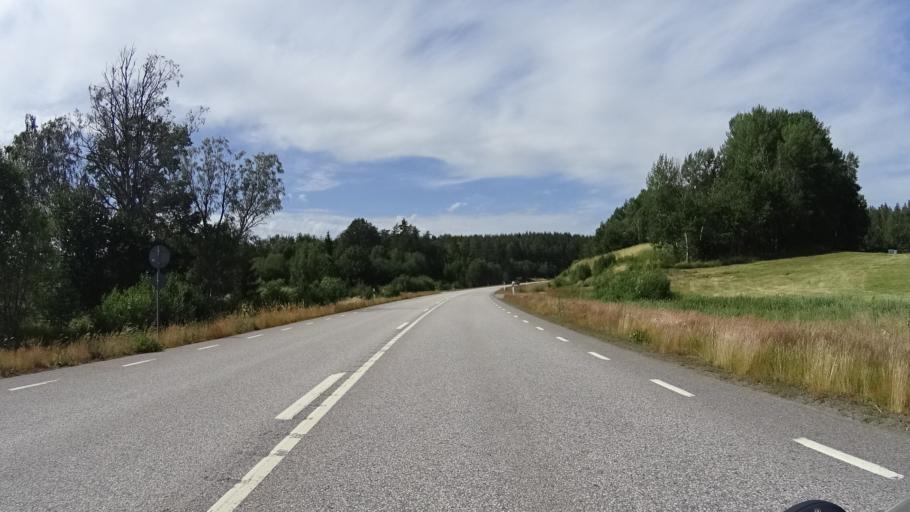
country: SE
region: Kalmar
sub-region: Vasterviks Kommun
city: Overum
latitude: 57.9669
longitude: 16.3405
